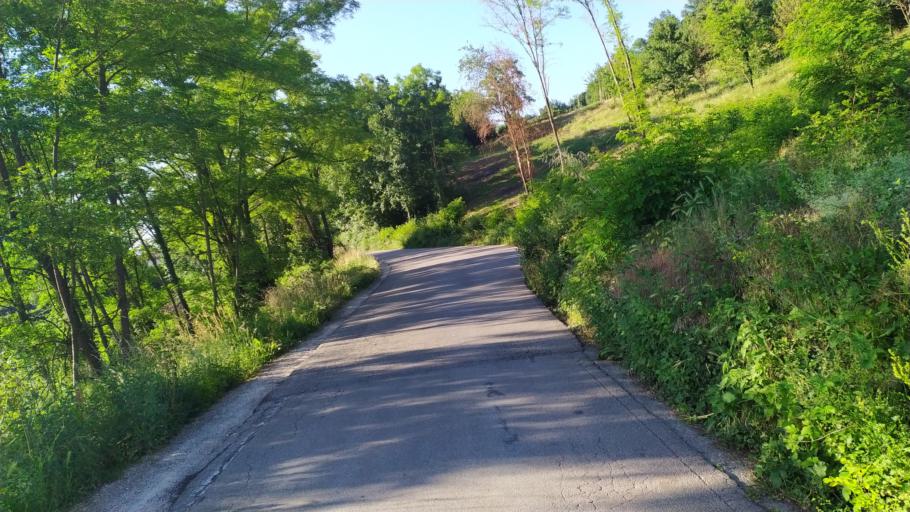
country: IT
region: Veneto
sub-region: Provincia di Vicenza
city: Malo
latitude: 45.6476
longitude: 11.4168
